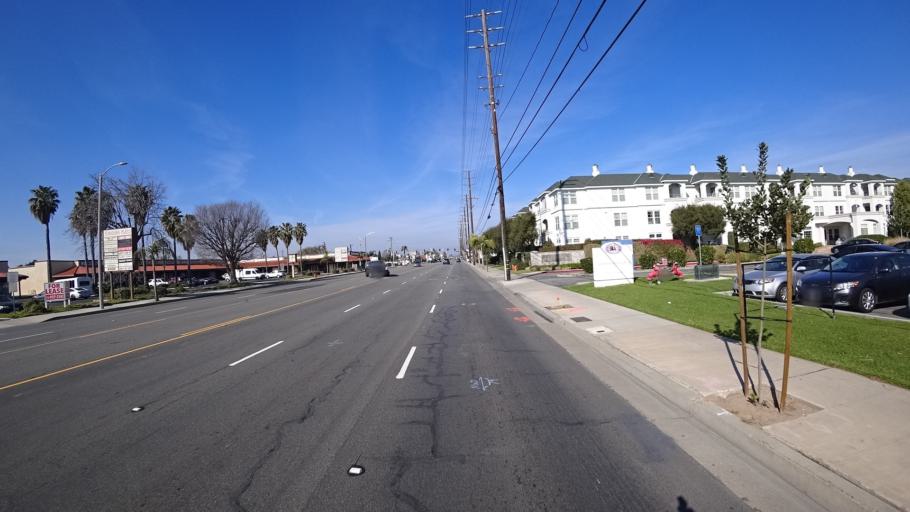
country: US
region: California
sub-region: Orange County
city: Orange
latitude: 33.7825
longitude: -117.8357
